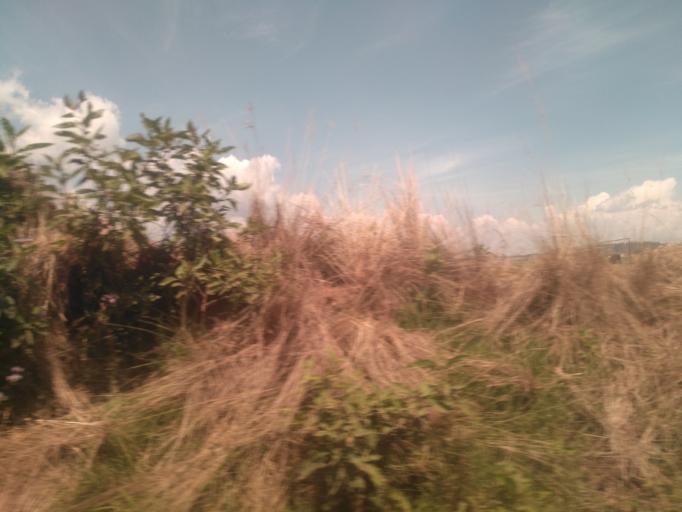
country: UG
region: Central Region
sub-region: Wakiso District
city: Entebbe
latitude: 0.0368
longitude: 32.4306
